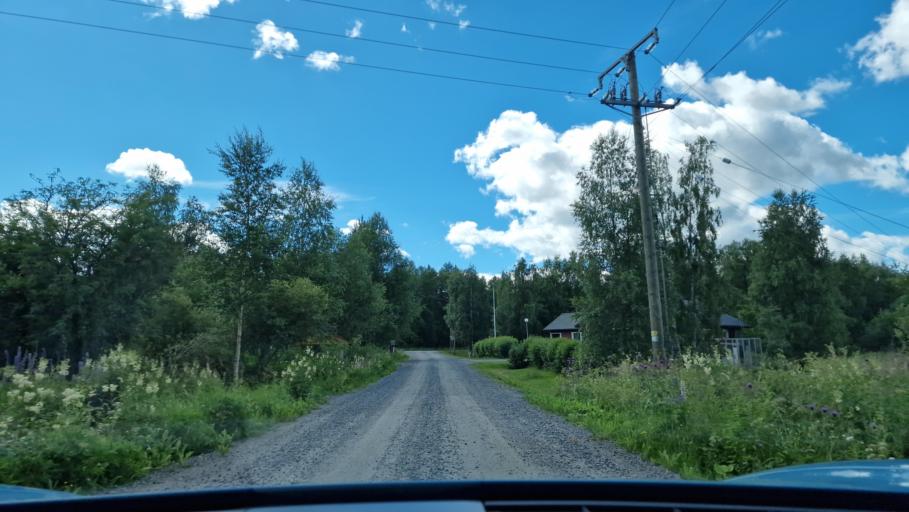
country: FI
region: Southern Ostrobothnia
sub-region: Jaerviseutu
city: Soini
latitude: 62.8452
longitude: 24.3245
